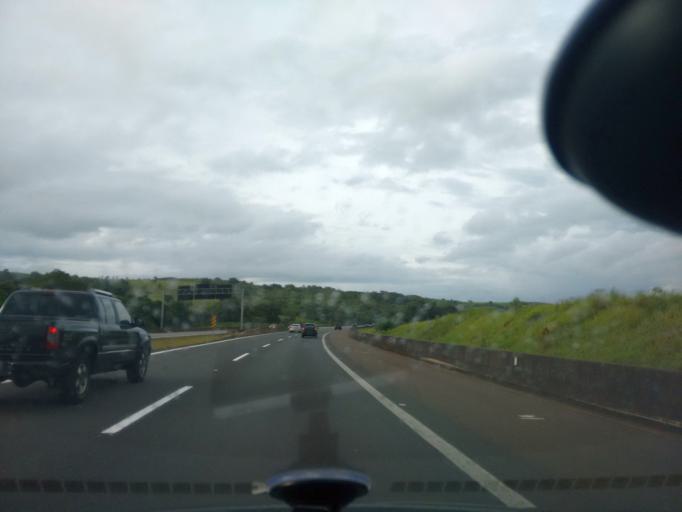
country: BR
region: Sao Paulo
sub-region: Limeira
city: Limeira
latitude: -22.5449
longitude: -47.4615
